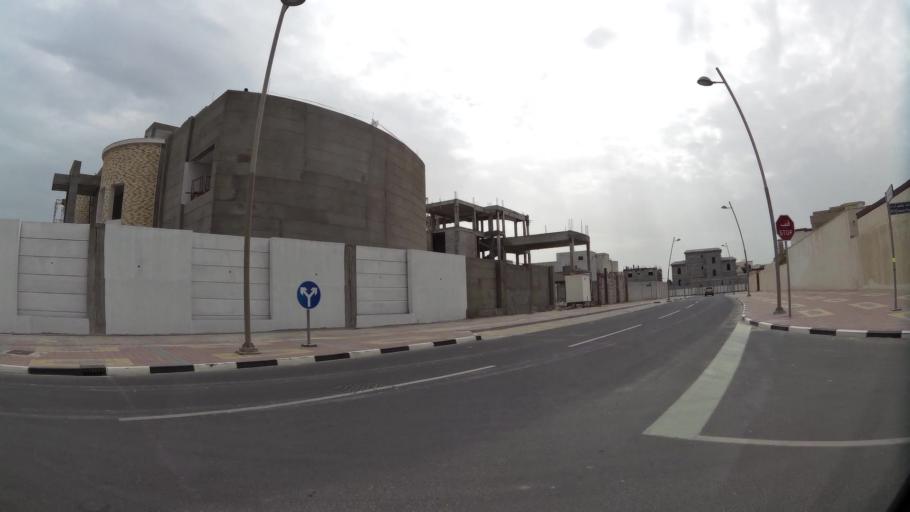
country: QA
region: Baladiyat ad Dawhah
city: Doha
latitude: 25.3440
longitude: 51.4869
